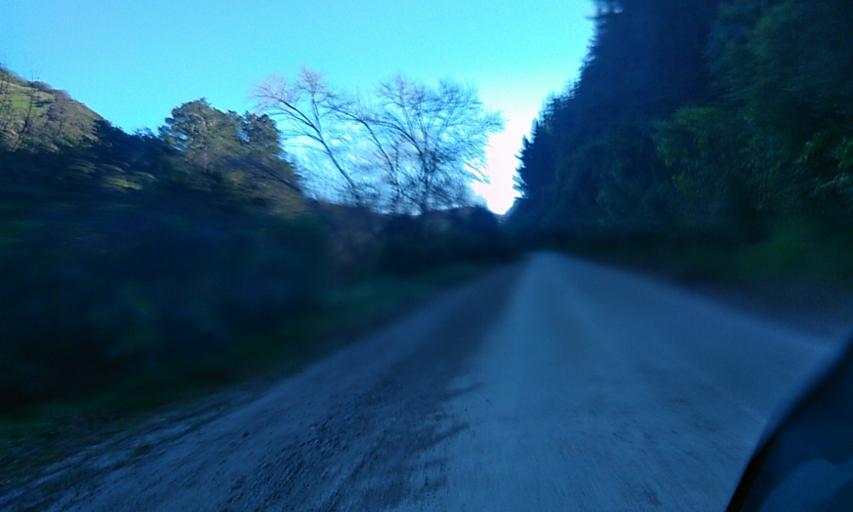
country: NZ
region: Gisborne
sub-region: Gisborne District
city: Gisborne
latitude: -38.5304
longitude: 178.0376
